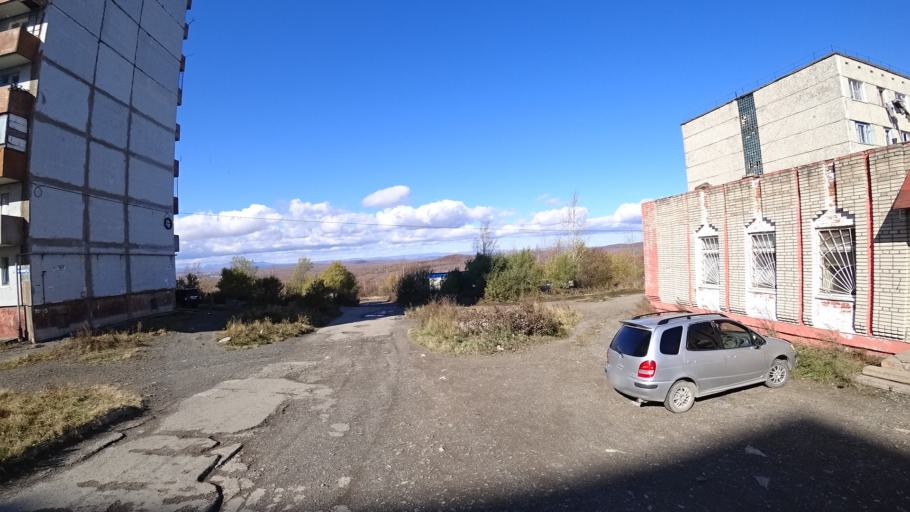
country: RU
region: Khabarovsk Krai
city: Amursk
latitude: 50.2426
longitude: 136.9039
